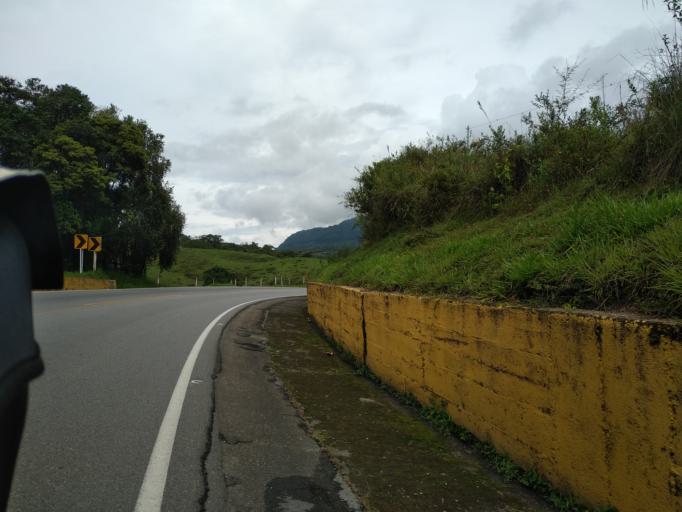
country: CO
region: Santander
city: Suaita
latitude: 6.0978
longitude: -73.3732
